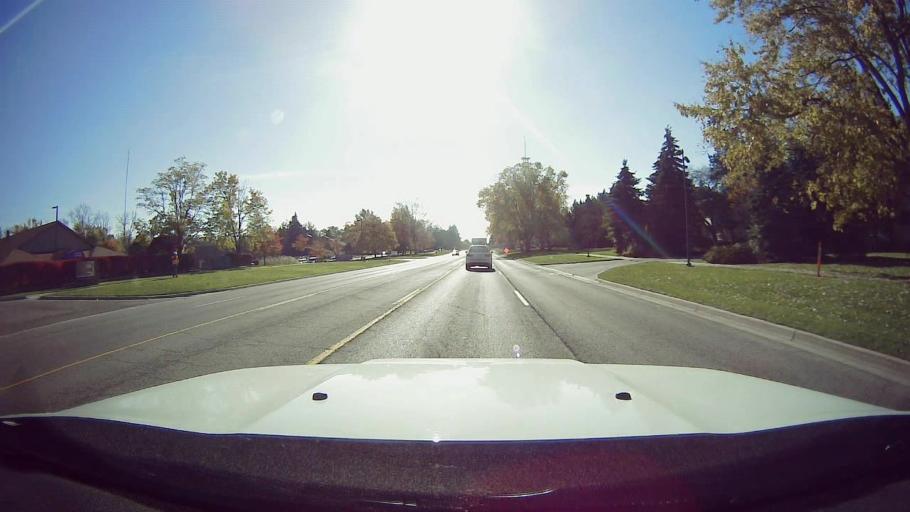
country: US
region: Michigan
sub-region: Oakland County
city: Southfield
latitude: 42.4773
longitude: -83.2610
